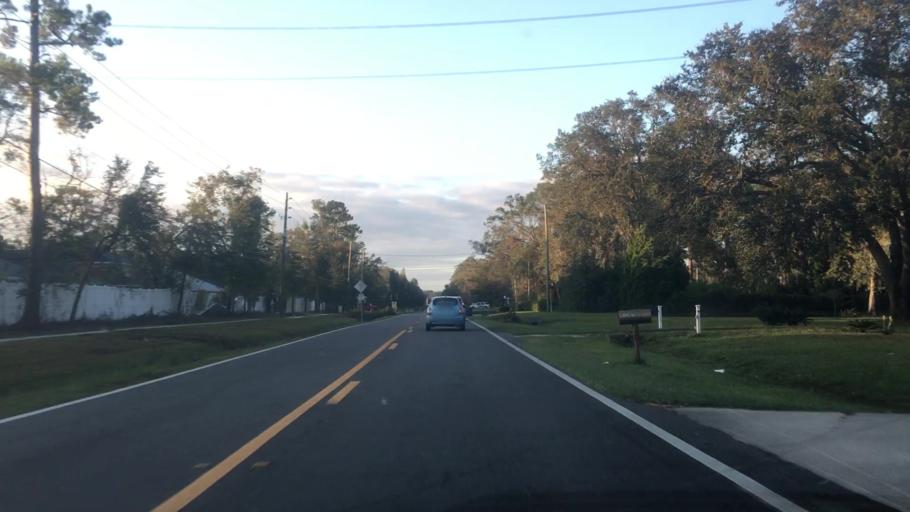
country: US
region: Florida
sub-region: Duval County
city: Jacksonville
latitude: 30.4692
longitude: -81.5795
